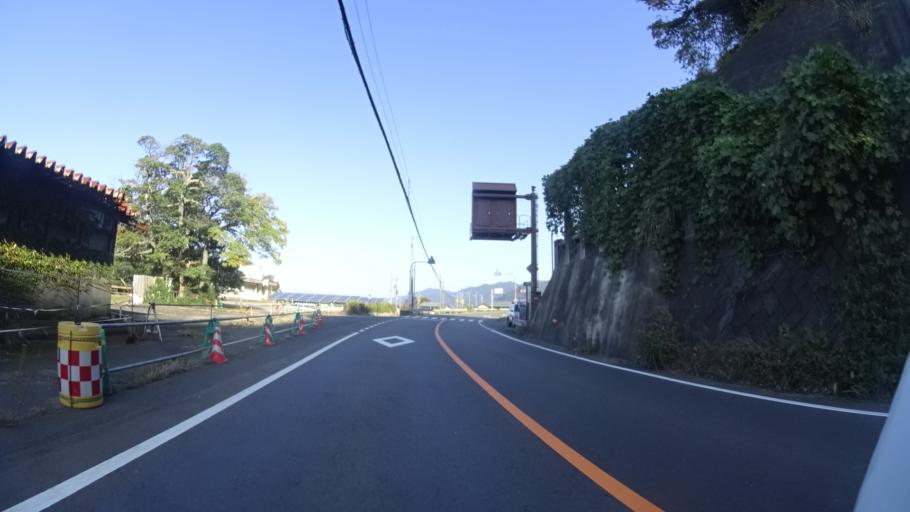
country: JP
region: Fukui
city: Tsuruga
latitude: 35.7347
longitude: 136.0977
